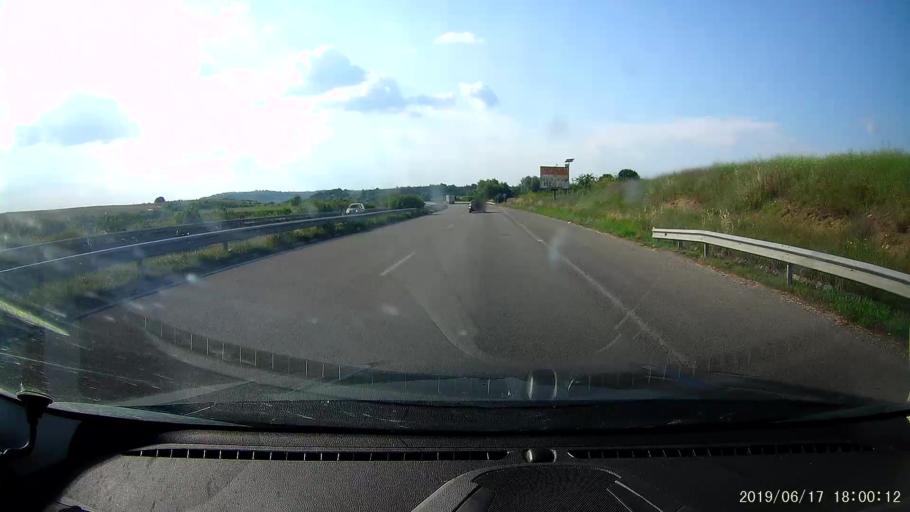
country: BG
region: Khaskovo
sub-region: Obshtina Svilengrad
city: Svilengrad
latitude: 41.7330
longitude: 26.2829
